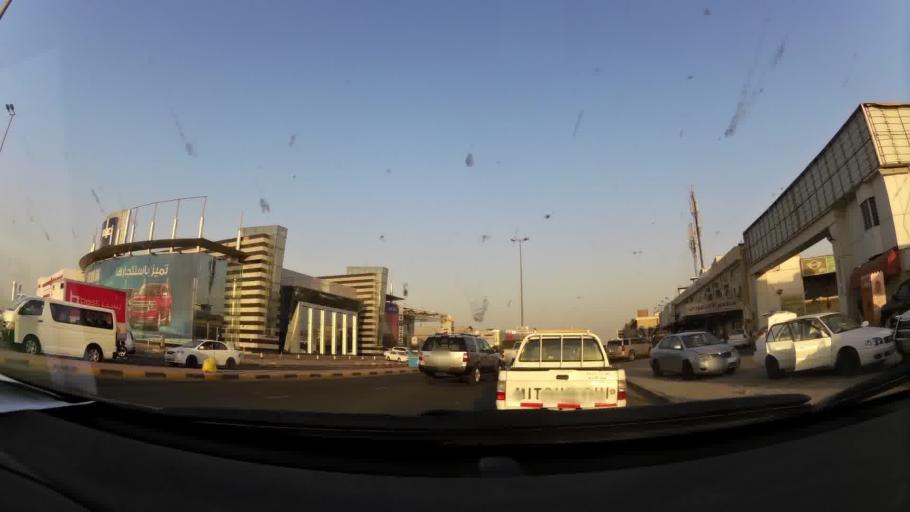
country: KW
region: Al Asimah
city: Ar Rabiyah
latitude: 29.3077
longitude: 47.9273
